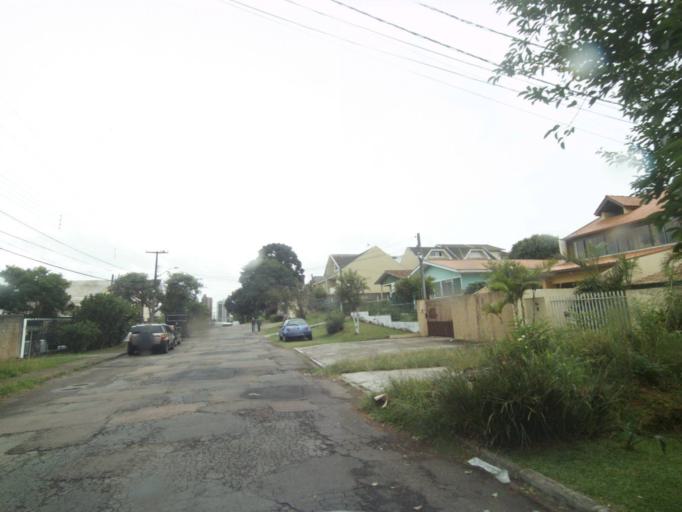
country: BR
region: Parana
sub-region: Curitiba
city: Curitiba
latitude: -25.4280
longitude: -49.3292
